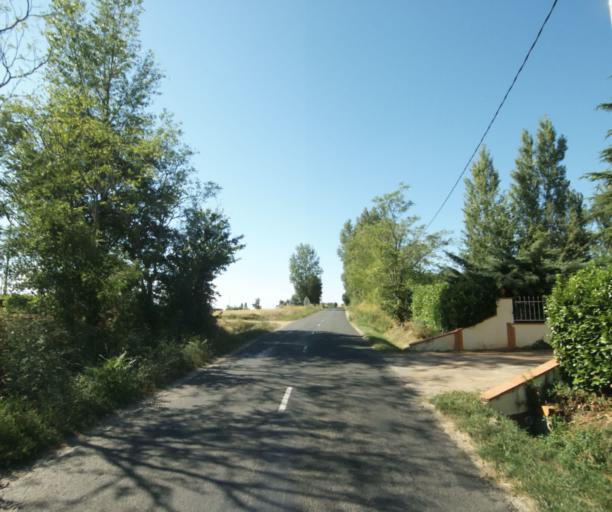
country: FR
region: Midi-Pyrenees
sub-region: Departement de la Haute-Garonne
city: Saint-Felix-Lauragais
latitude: 43.5177
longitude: 1.9298
